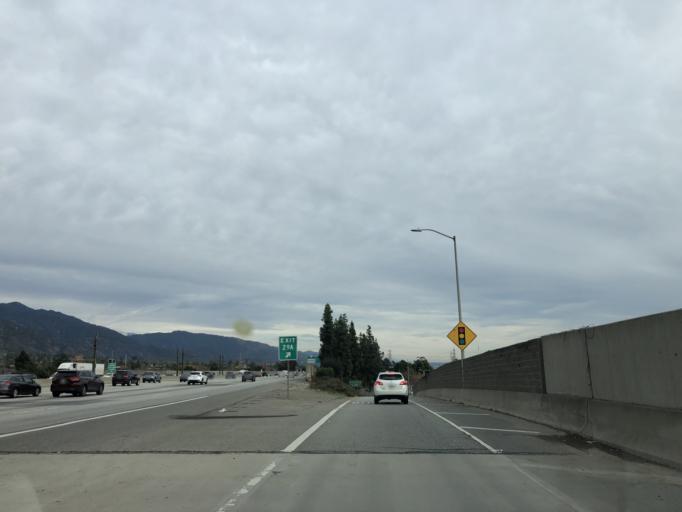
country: US
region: California
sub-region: Los Angeles County
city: East Pasadena
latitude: 34.1522
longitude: -118.0985
